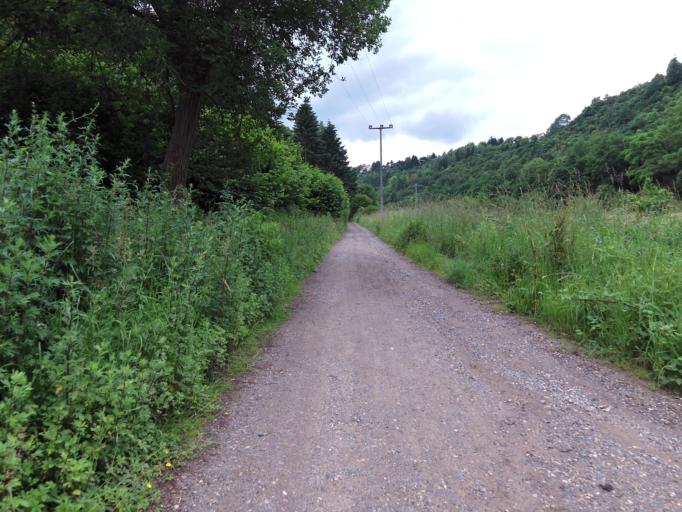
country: DE
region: Rheinland-Pfalz
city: Bobenheim am Berg
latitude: 49.5299
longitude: 8.1450
